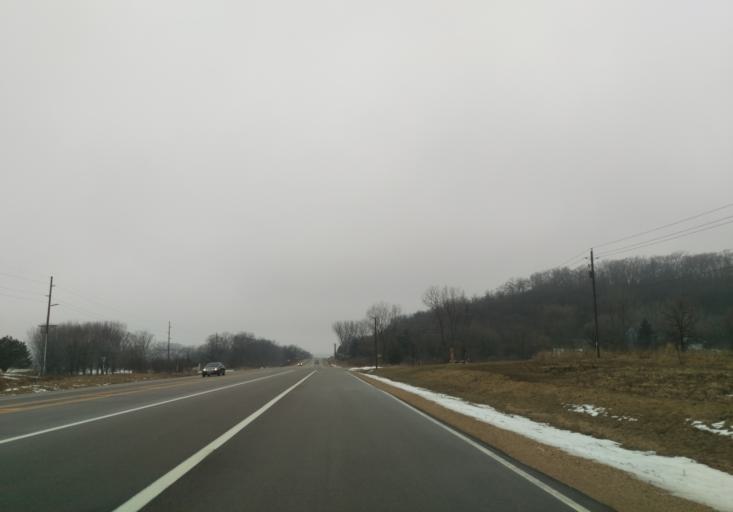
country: US
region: Wisconsin
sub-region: Dane County
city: Cross Plains
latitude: 43.0969
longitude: -89.6185
